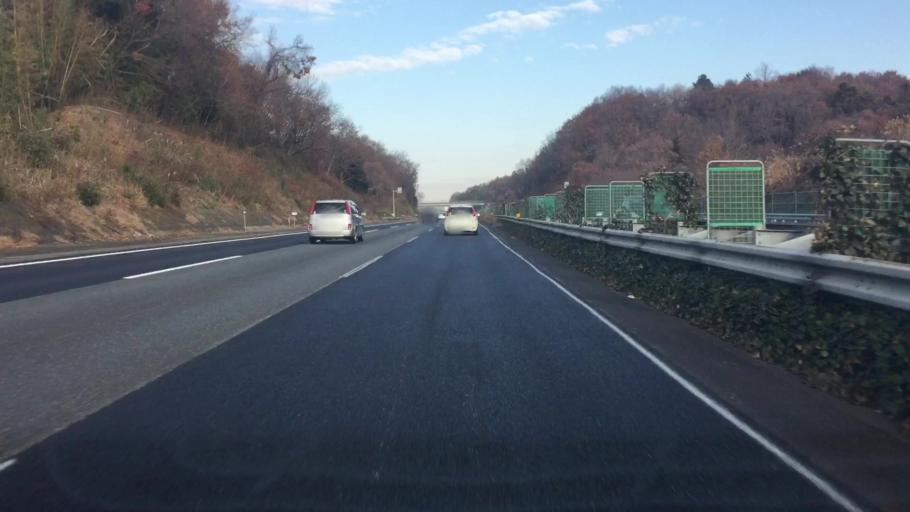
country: JP
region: Saitama
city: Ogawa
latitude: 36.0931
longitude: 139.2856
